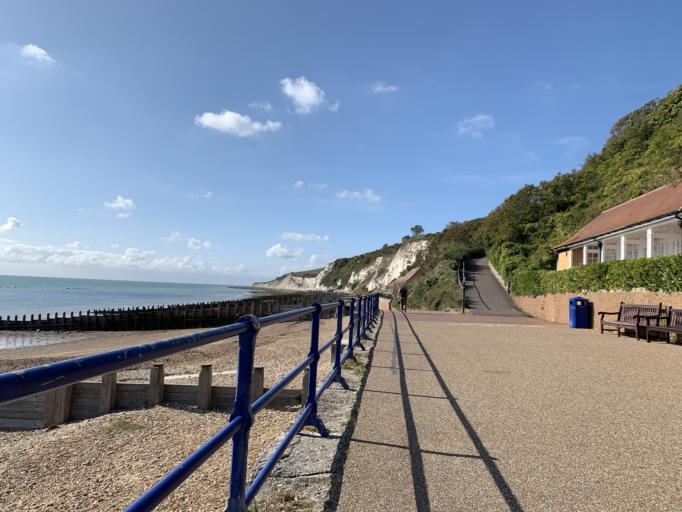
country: GB
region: England
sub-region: East Sussex
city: Eastbourne
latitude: 50.7544
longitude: 0.2742
